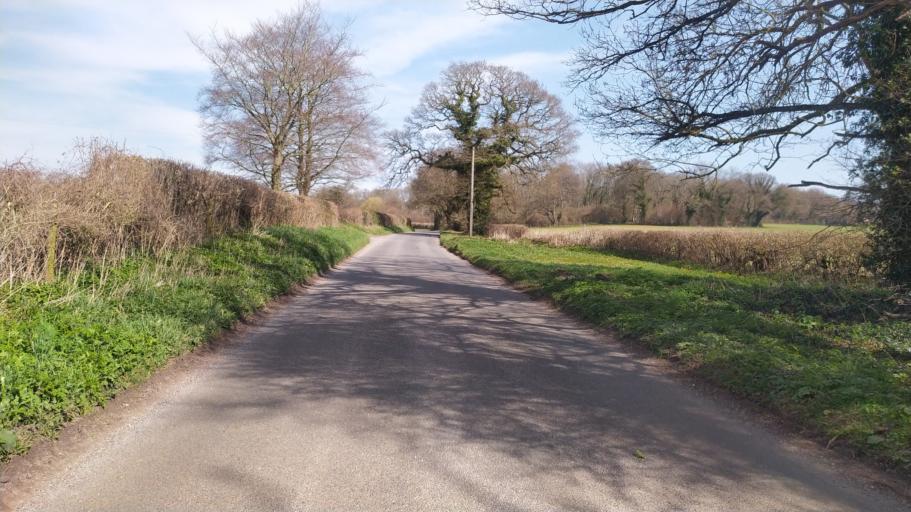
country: GB
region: England
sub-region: Hampshire
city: Four Marks
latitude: 51.0548
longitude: -1.1151
